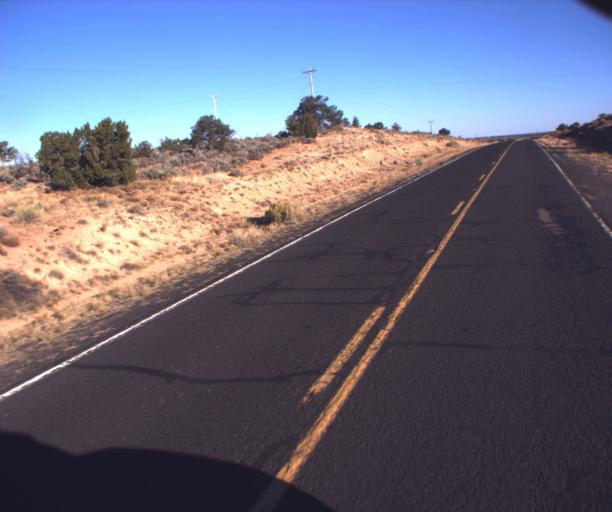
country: US
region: Arizona
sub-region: Apache County
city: Ganado
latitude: 35.6587
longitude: -109.5489
